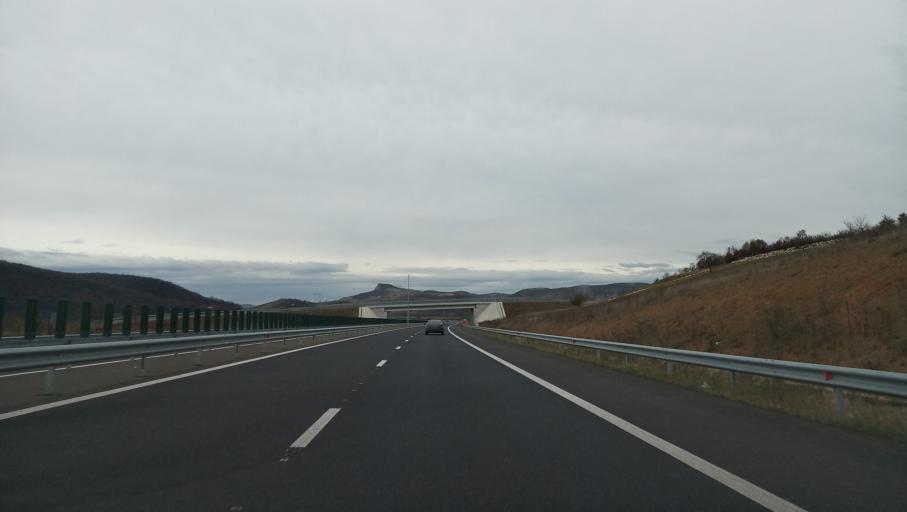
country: RO
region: Hunedoara
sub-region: Comuna Branisca
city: Branisca
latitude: 45.9290
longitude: 22.7664
